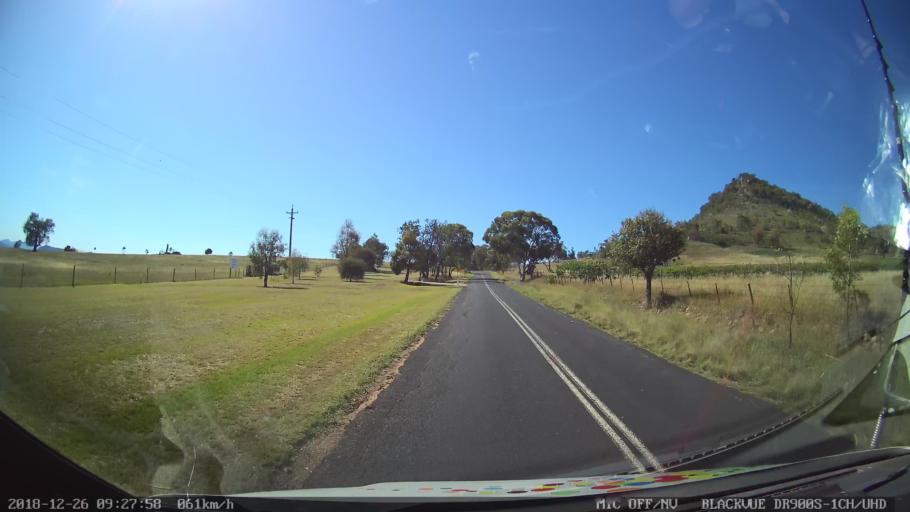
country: AU
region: New South Wales
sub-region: Mid-Western Regional
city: Kandos
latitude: -32.8410
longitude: 150.0195
